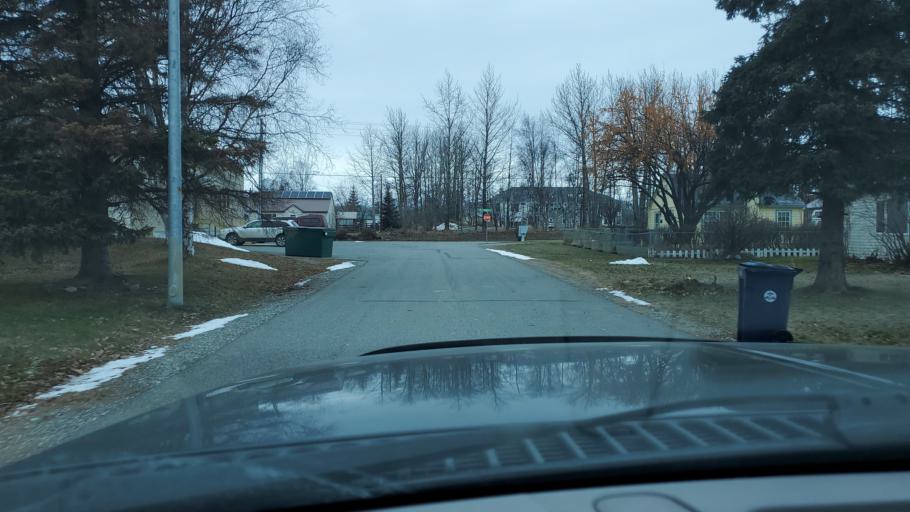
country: US
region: Alaska
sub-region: Matanuska-Susitna Borough
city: Palmer
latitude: 61.5971
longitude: -149.1093
